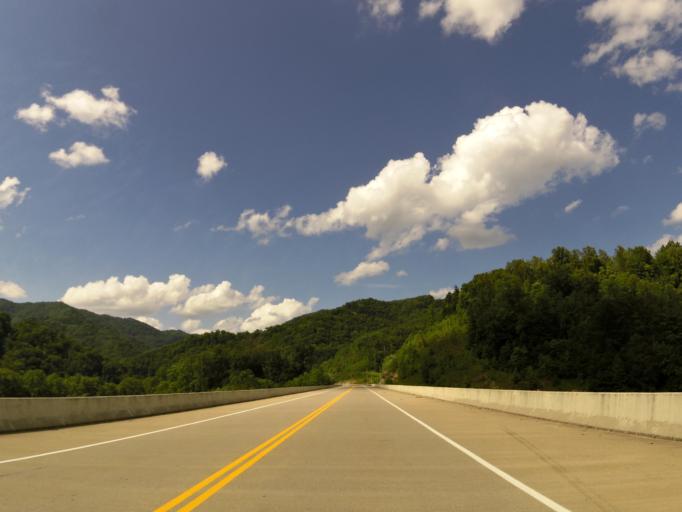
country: US
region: Kentucky
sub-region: Harlan County
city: Harlan
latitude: 36.8057
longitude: -83.2707
